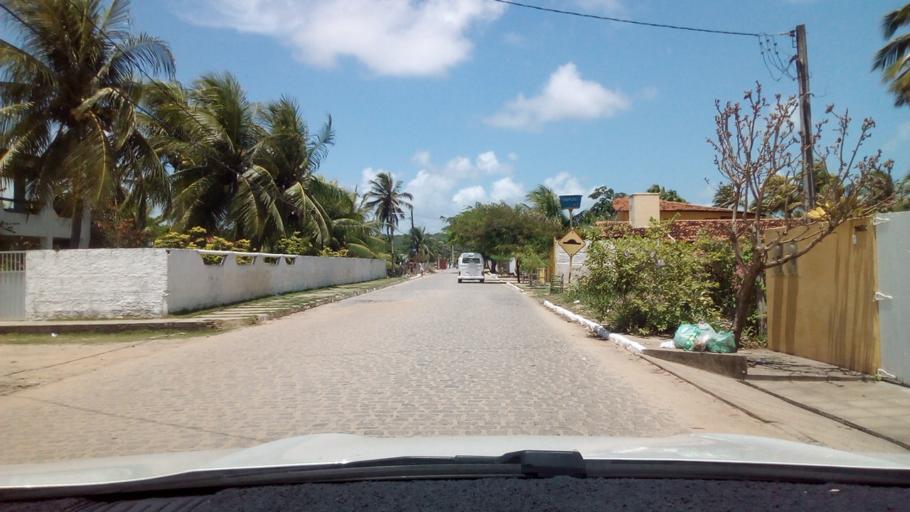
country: BR
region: Paraiba
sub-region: Pitimbu
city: Pitimbu
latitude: -7.4977
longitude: -34.8143
